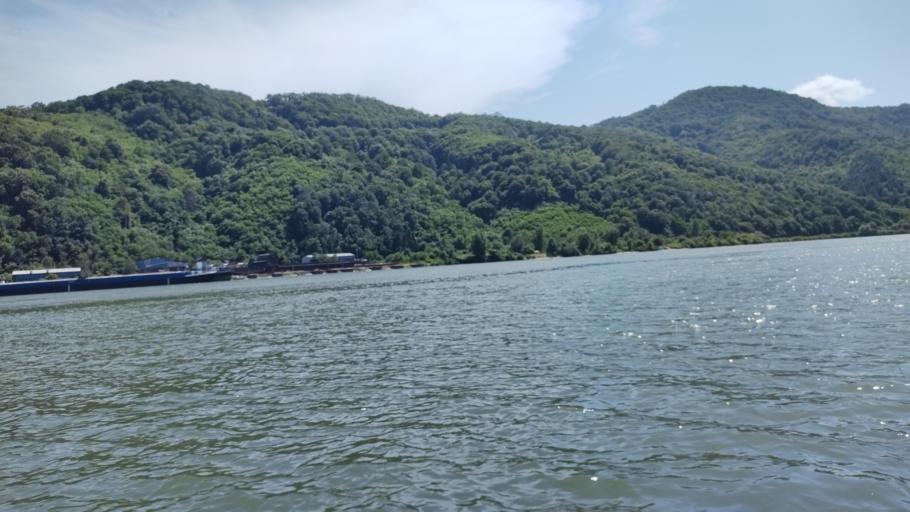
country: RS
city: Radenka
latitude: 44.6591
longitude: 21.7598
